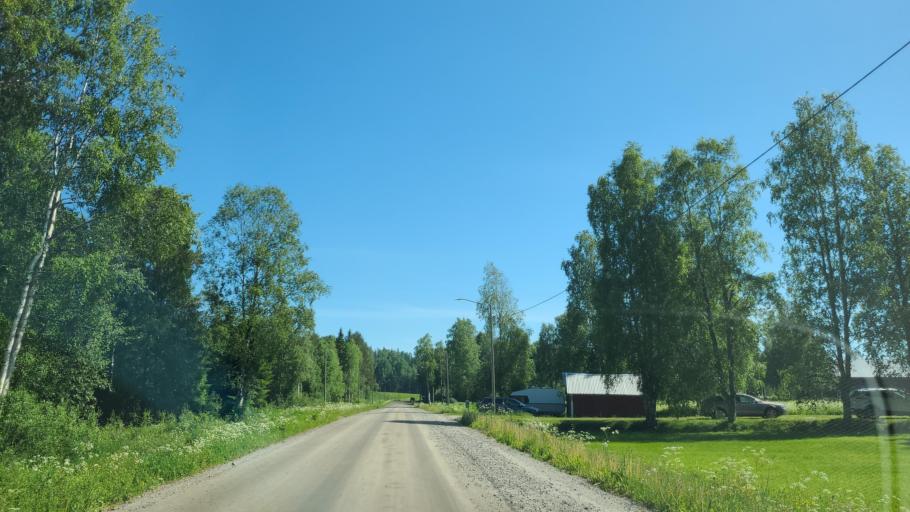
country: SE
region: Vaesterbotten
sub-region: Bjurholms Kommun
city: Bjurholm
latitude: 63.6964
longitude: 18.9525
